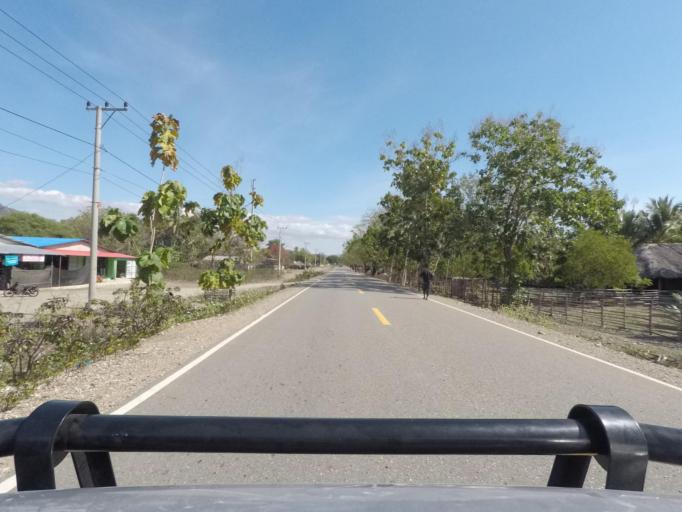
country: ID
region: East Nusa Tenggara
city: Atambua
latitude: -8.9016
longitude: 124.9987
